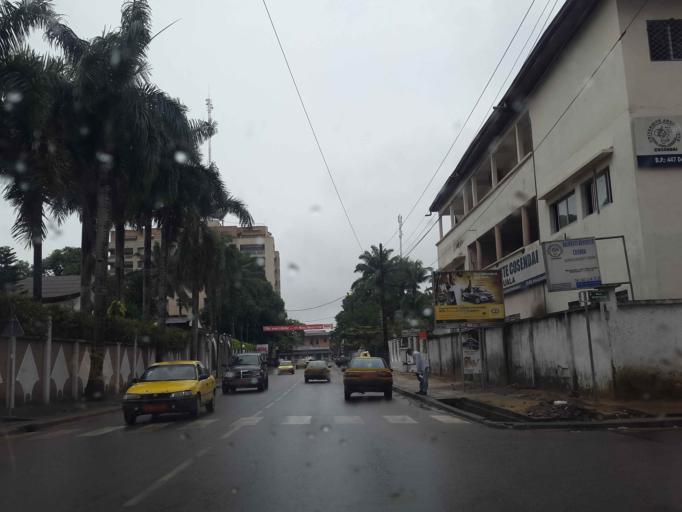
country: CM
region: Littoral
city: Douala
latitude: 4.0380
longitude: 9.6937
